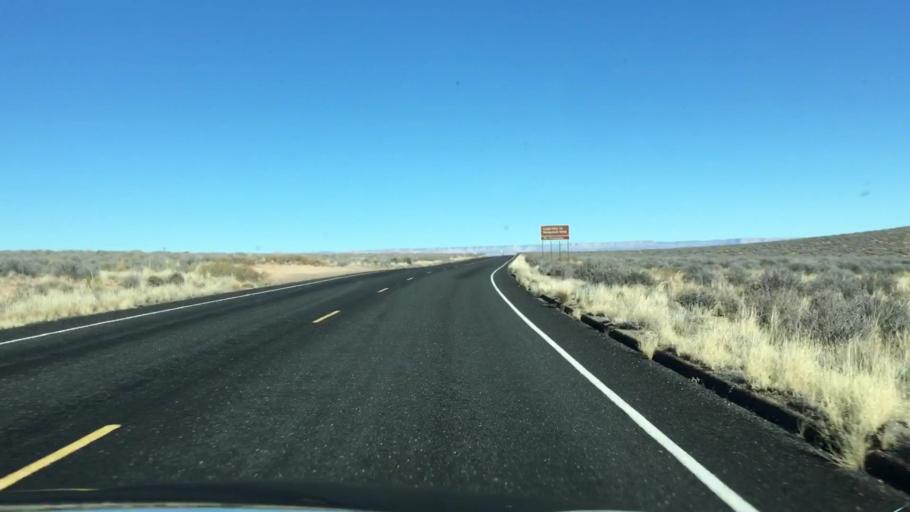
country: US
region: Arizona
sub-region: Coconino County
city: Page
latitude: 36.9850
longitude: -111.5237
